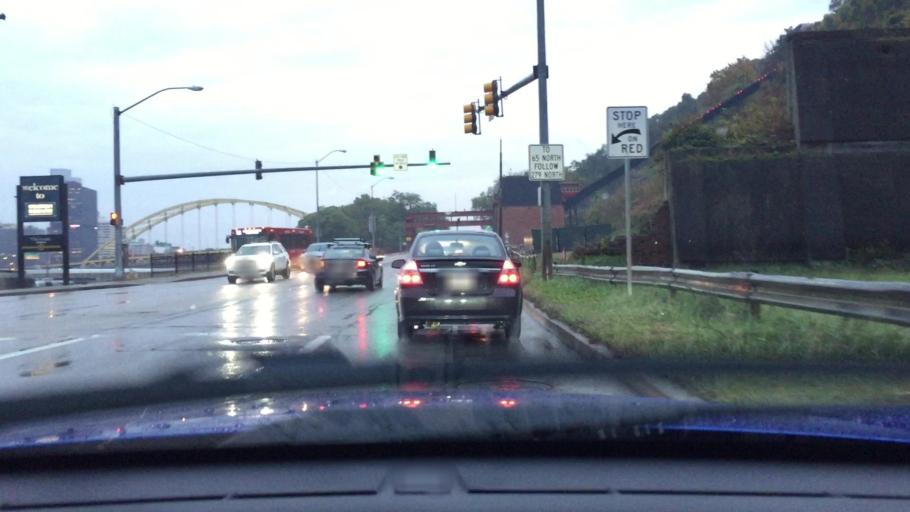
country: US
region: Pennsylvania
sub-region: Allegheny County
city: Pittsburgh
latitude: 40.4408
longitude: -80.0192
